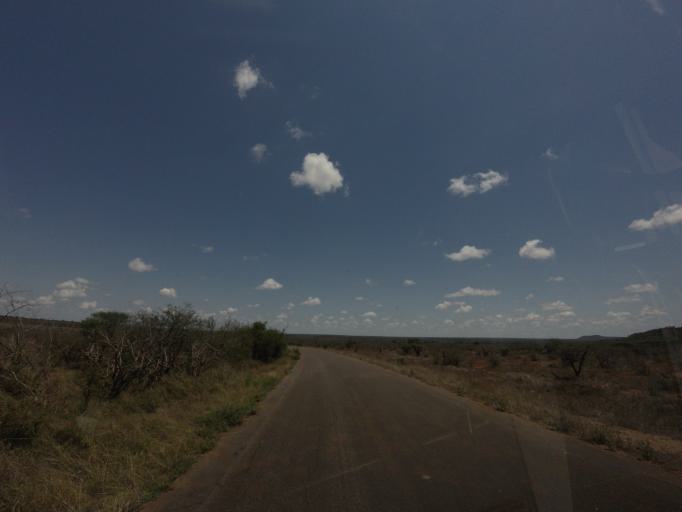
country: ZA
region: Mpumalanga
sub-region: Ehlanzeni District
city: Komatipoort
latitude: -24.8257
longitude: 31.8921
